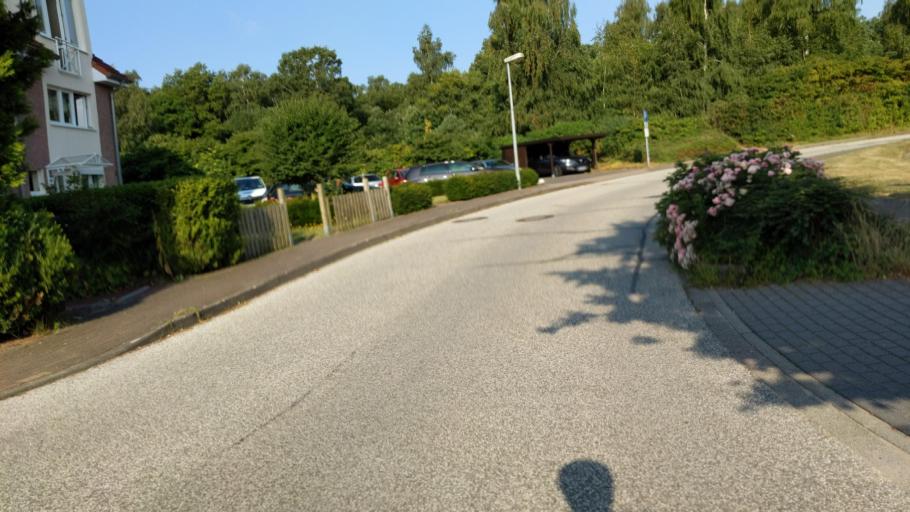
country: DE
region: Mecklenburg-Vorpommern
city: Selmsdorf
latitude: 53.8830
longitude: 10.8392
